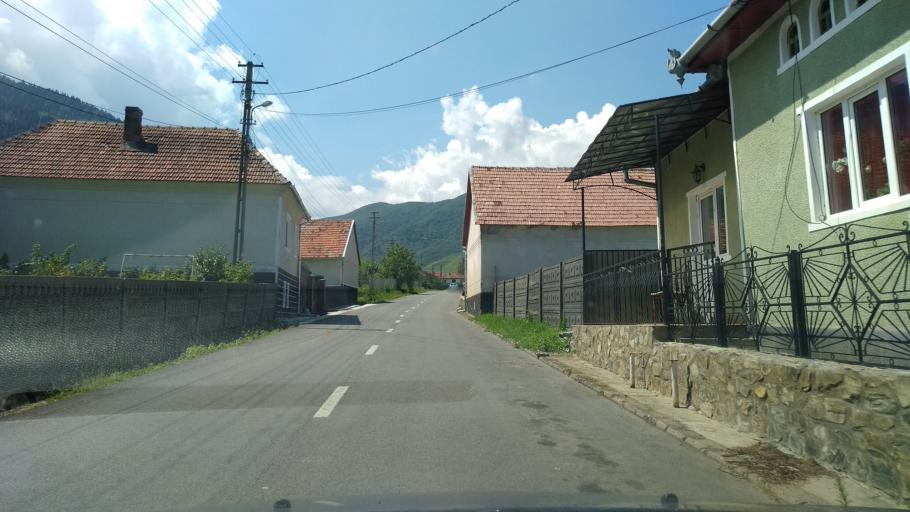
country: RO
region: Hunedoara
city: Salasu de Sus
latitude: 45.4801
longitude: 22.9154
